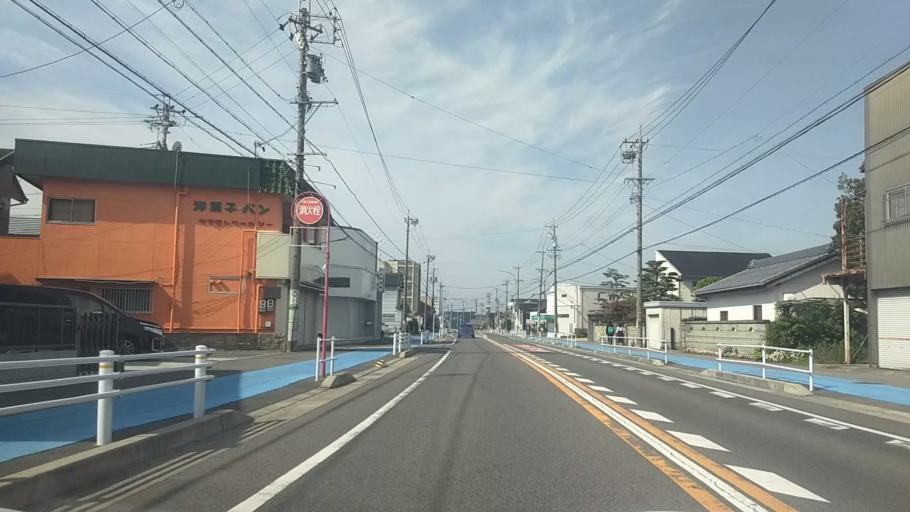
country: JP
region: Aichi
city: Okazaki
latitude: 34.9484
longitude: 137.1579
